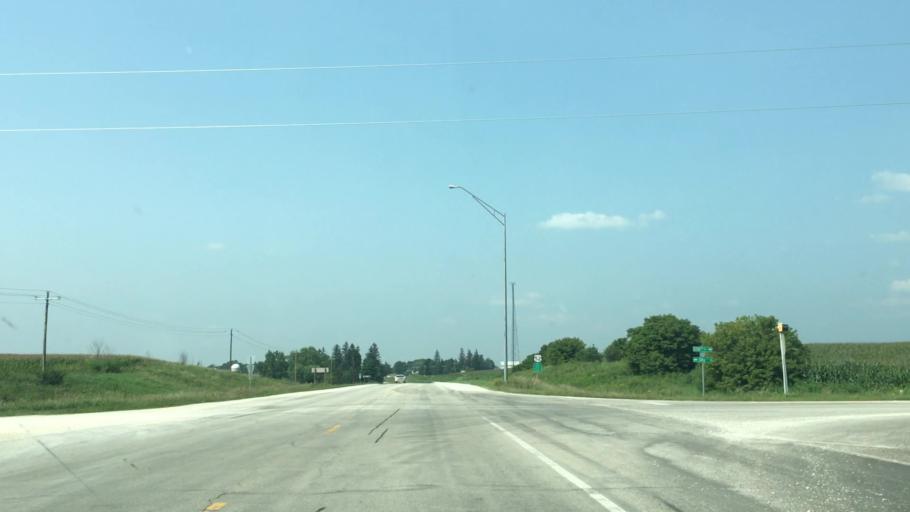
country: US
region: Iowa
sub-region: Winneshiek County
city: Decorah
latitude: 43.4429
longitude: -91.8620
